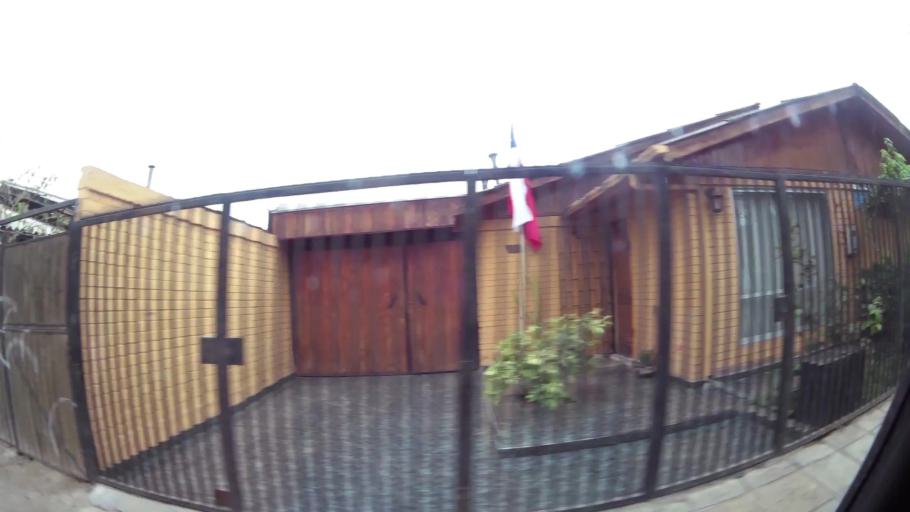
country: CL
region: Santiago Metropolitan
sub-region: Provincia de Santiago
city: Lo Prado
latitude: -33.4952
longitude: -70.7591
